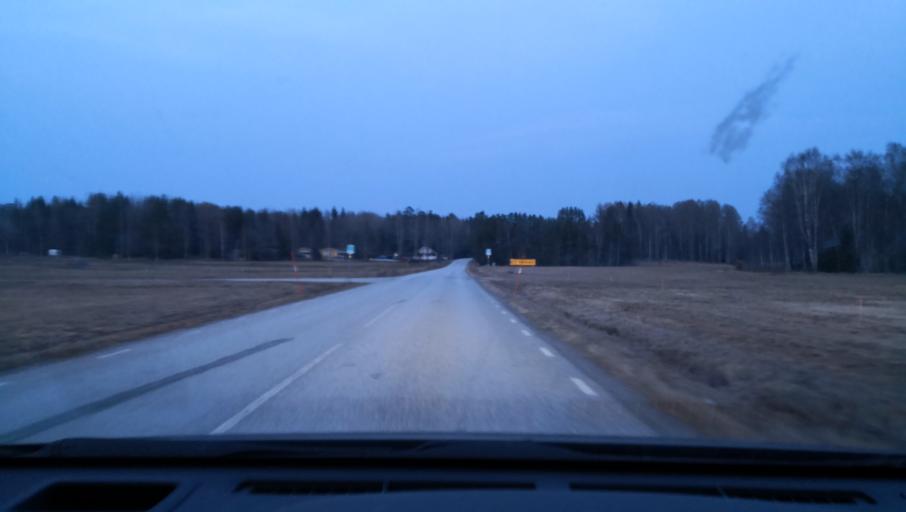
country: SE
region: OErebro
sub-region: Lindesbergs Kommun
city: Lindesberg
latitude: 59.5984
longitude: 15.3482
